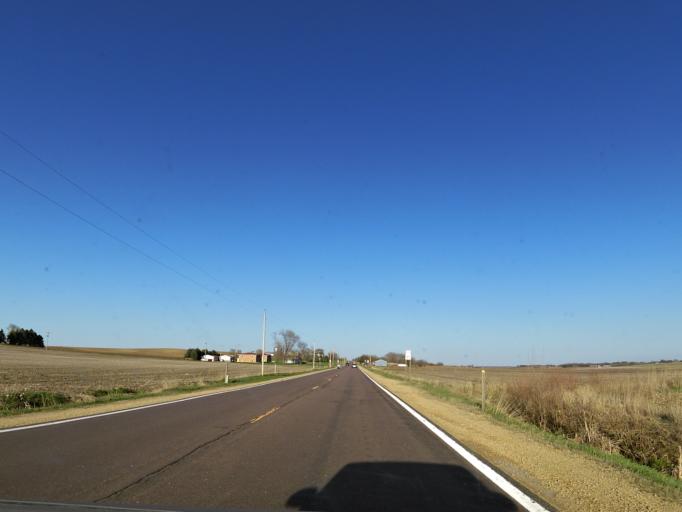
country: US
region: Minnesota
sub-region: Goodhue County
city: Cannon Falls
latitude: 44.6013
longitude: -92.9575
